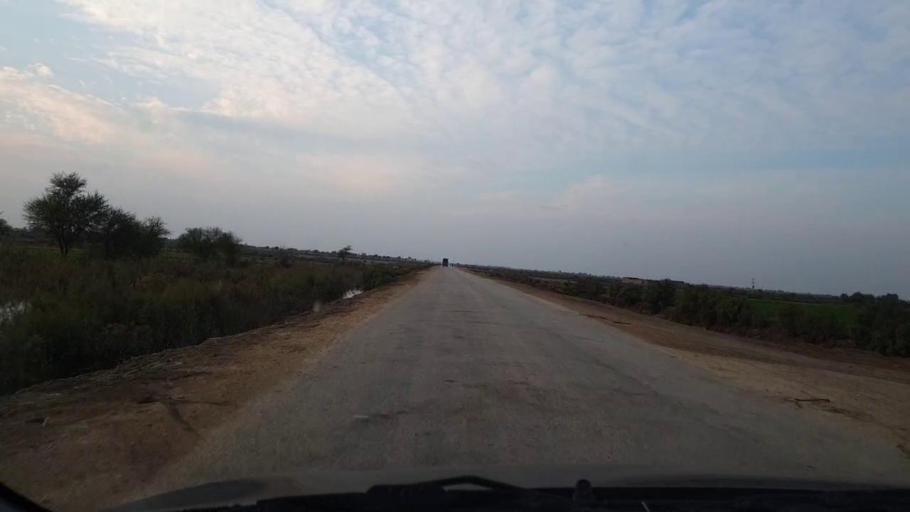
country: PK
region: Sindh
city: Sinjhoro
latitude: 25.9987
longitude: 68.8478
